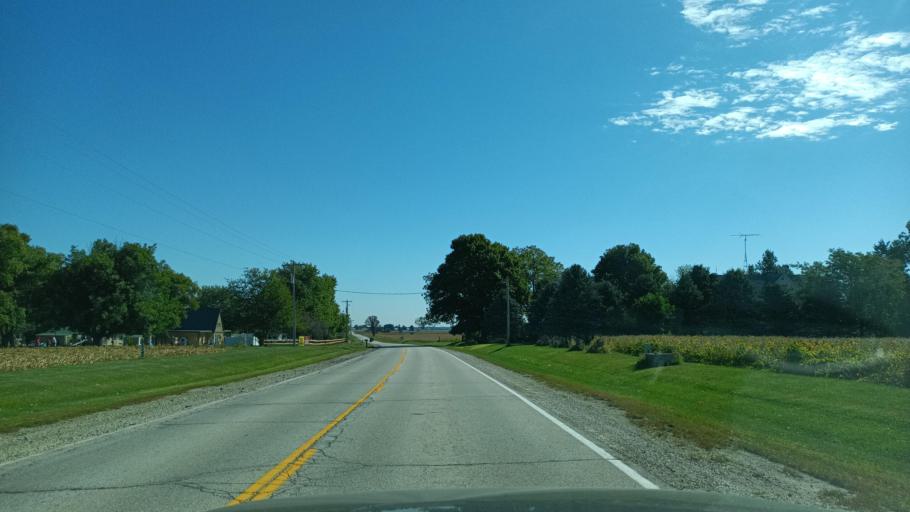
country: US
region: Illinois
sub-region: Knox County
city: Knoxville
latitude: 40.9078
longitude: -90.2376
